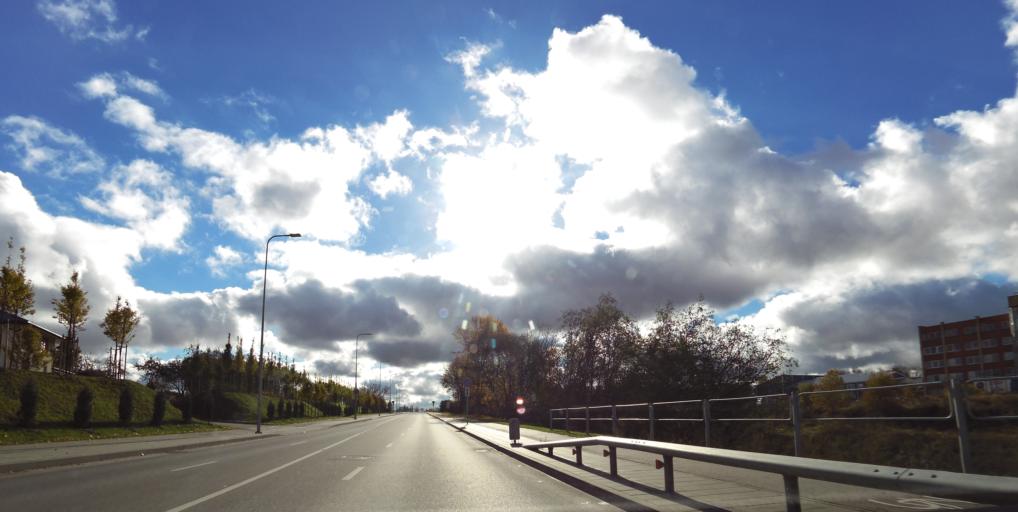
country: LT
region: Vilnius County
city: Naujamiestis
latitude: 54.6492
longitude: 25.2763
